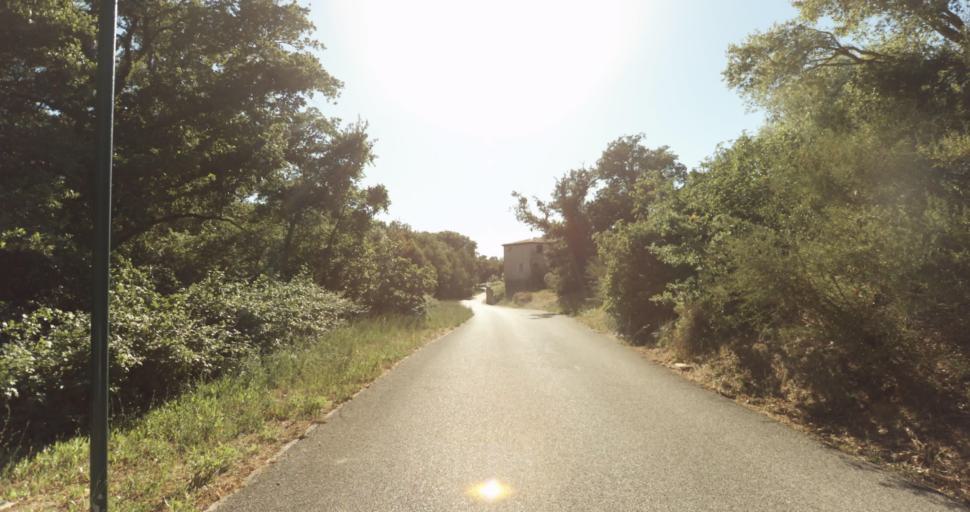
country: FR
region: Provence-Alpes-Cote d'Azur
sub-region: Departement du Var
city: Gassin
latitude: 43.2519
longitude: 6.6034
